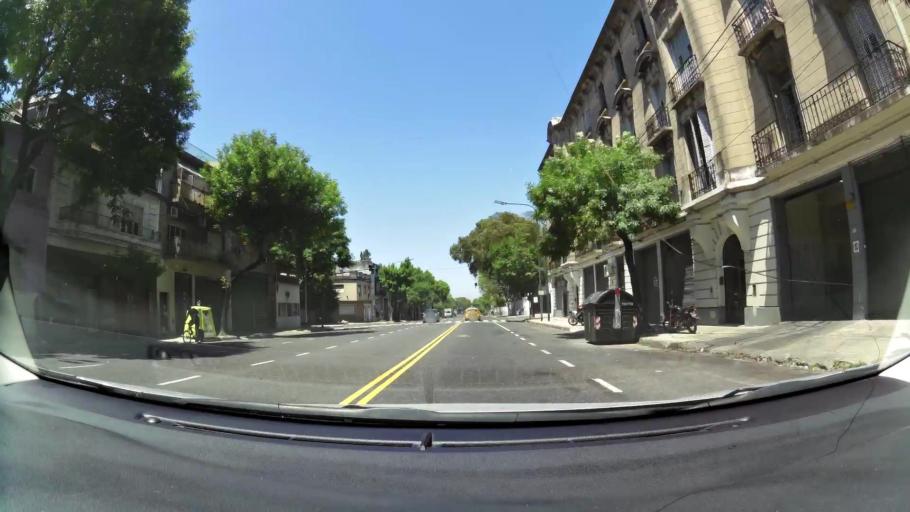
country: AR
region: Buenos Aires F.D.
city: Buenos Aires
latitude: -34.6374
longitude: -58.3901
